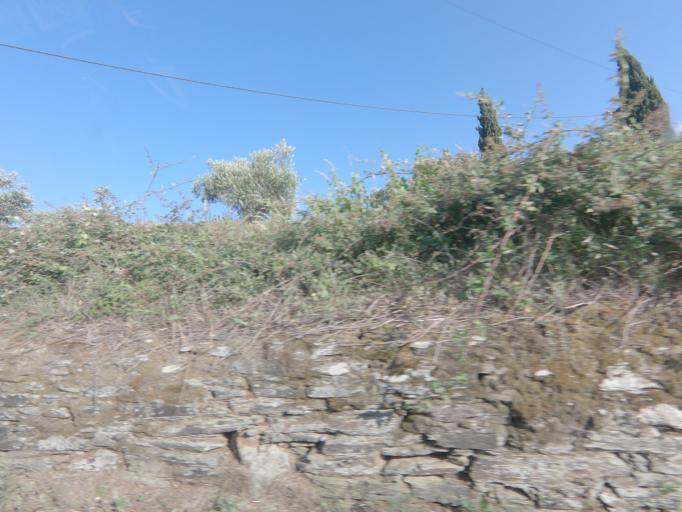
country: PT
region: Vila Real
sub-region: Sabrosa
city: Vilela
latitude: 41.1796
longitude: -7.6071
